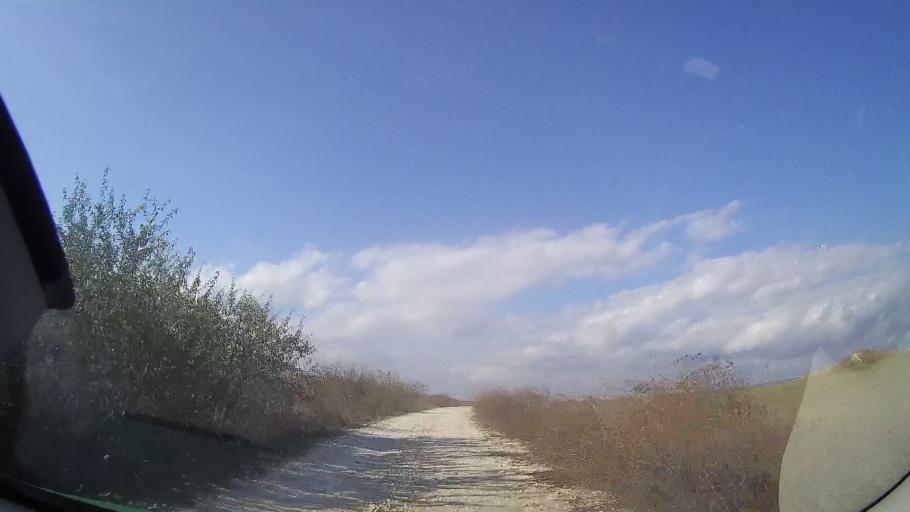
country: RO
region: Constanta
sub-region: Comuna Douazeci si Trei August
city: Douazeci si Trei August
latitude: 43.9047
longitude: 28.6171
